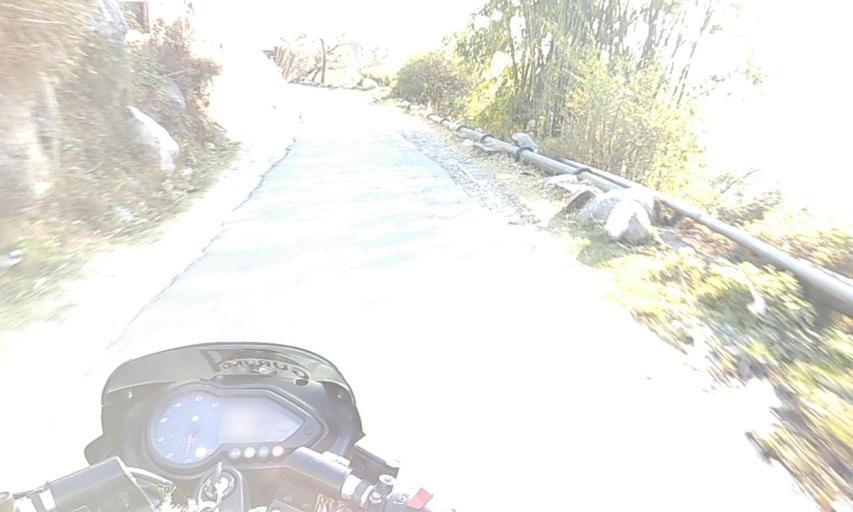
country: IN
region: Himachal Pradesh
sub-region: Kangra
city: Palampur
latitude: 32.1318
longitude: 76.5360
